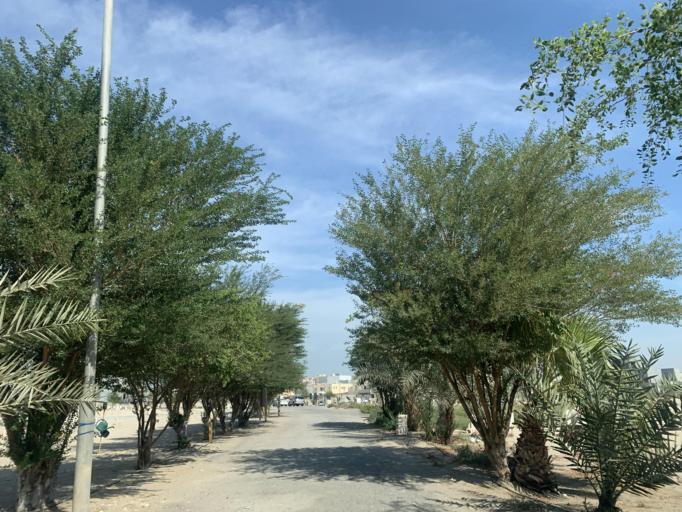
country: BH
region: Central Governorate
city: Madinat Hamad
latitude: 26.1142
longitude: 50.4849
